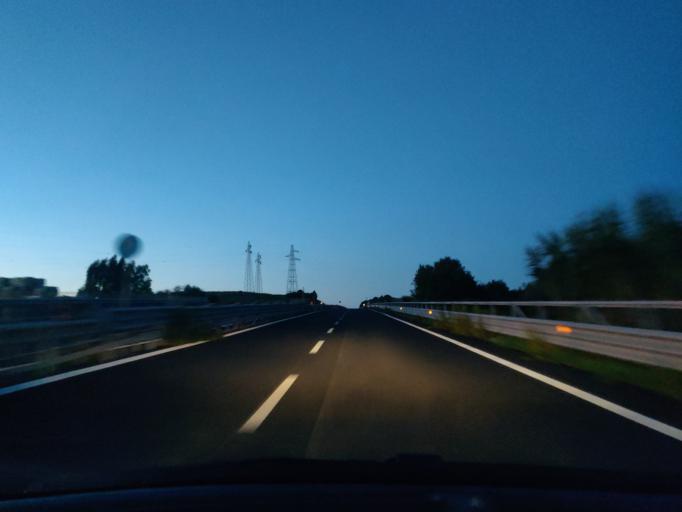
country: IT
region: Latium
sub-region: Citta metropolitana di Roma Capitale
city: Civitavecchia
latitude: 42.1101
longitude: 11.7927
